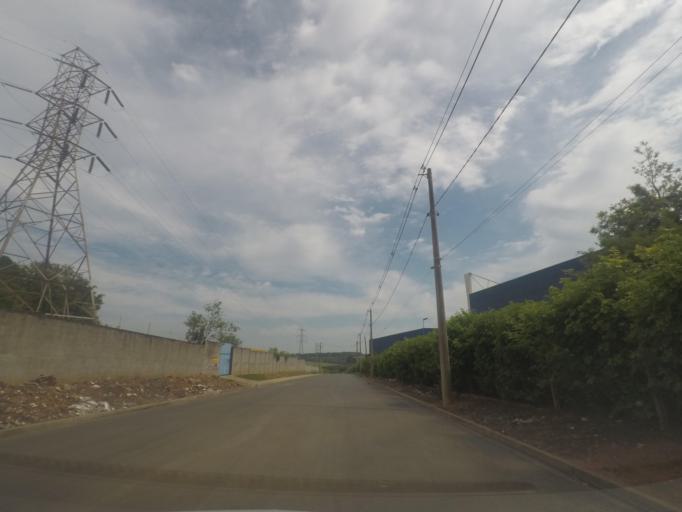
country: BR
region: Sao Paulo
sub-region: Sumare
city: Sumare
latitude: -22.8059
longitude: -47.2563
